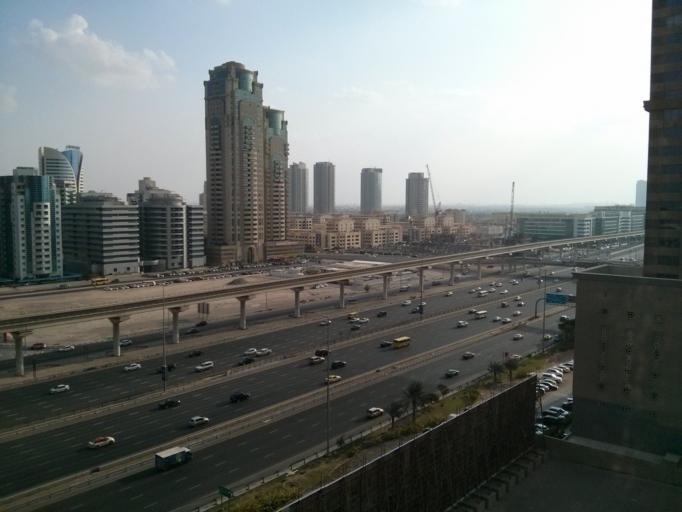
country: AE
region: Dubai
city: Dubai
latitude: 25.1482
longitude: 55.1953
